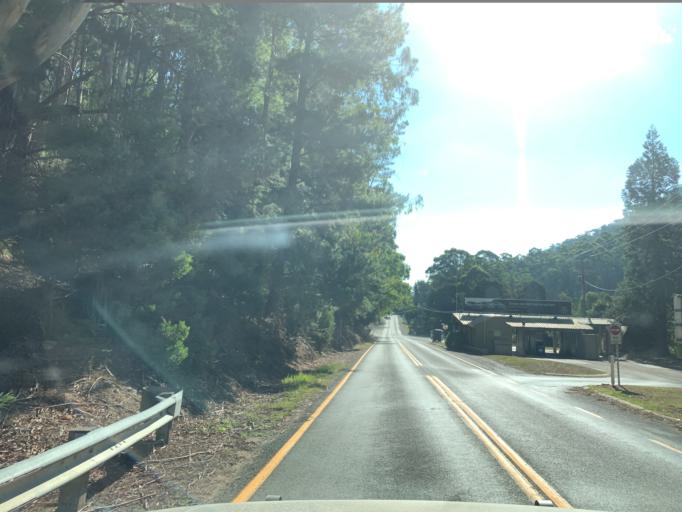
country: AU
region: Victoria
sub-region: Mansfield
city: Mansfield
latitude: -37.1106
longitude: 146.3998
